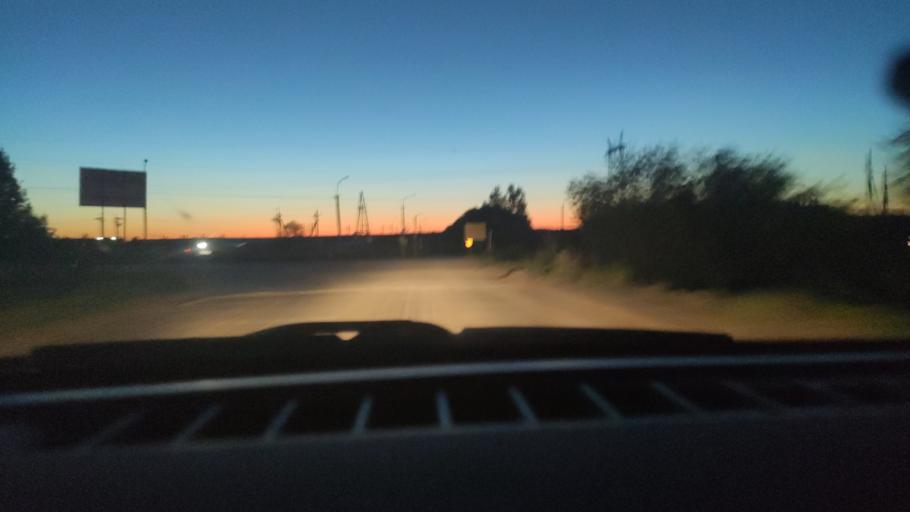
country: RU
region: Perm
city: Sylva
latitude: 58.0255
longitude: 56.7382
